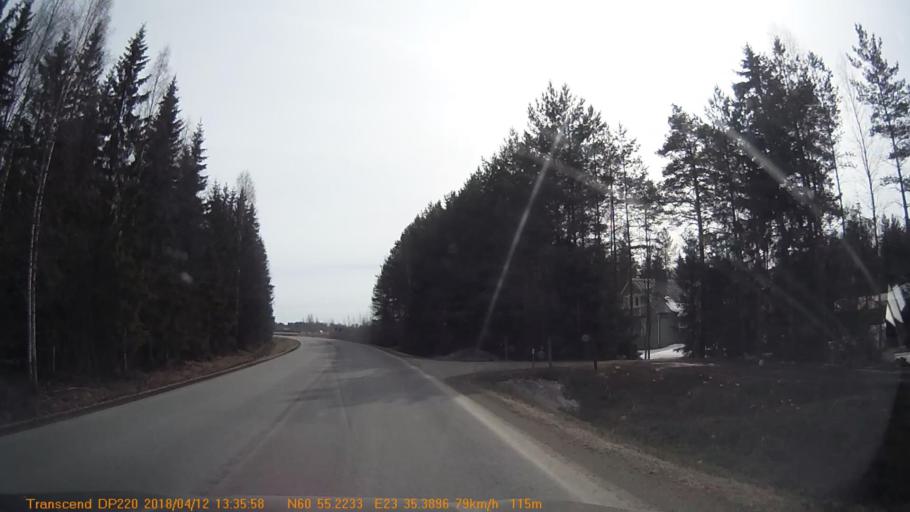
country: FI
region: Haeme
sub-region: Forssa
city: Forssa
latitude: 60.9203
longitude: 23.5899
